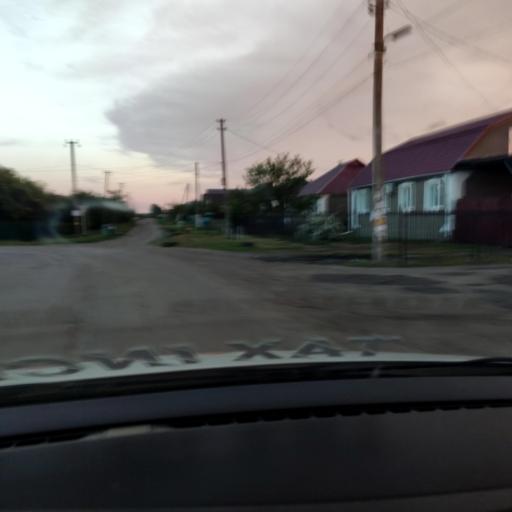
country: RU
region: Voronezj
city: Maslovka
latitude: 51.4527
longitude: 39.2401
